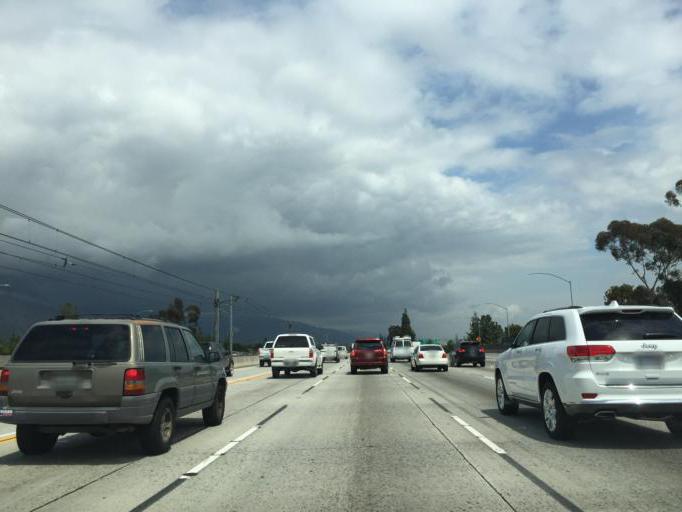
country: US
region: California
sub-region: Los Angeles County
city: East Pasadena
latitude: 34.1524
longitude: -118.1050
